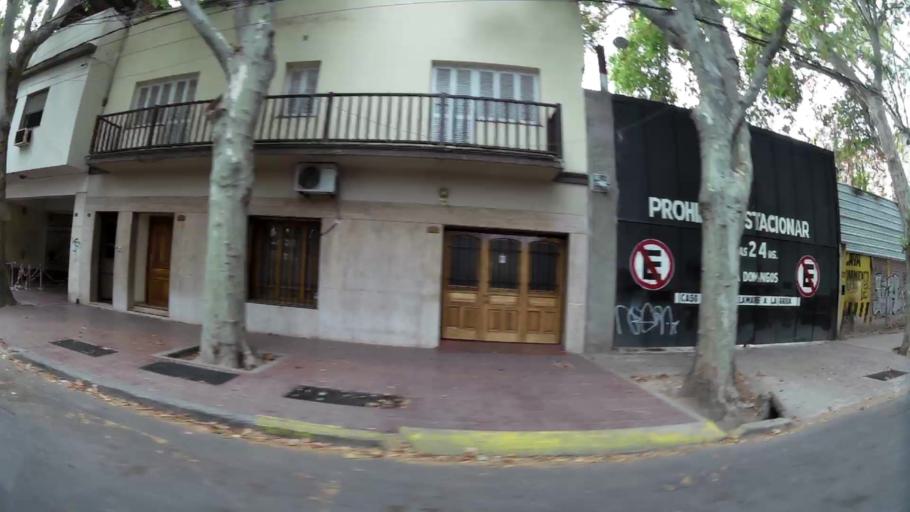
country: AR
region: Mendoza
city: Mendoza
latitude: -32.8829
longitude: -68.8400
